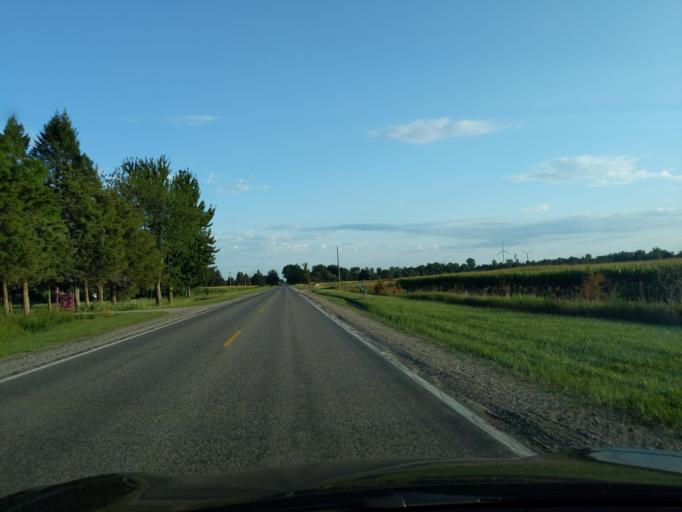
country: US
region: Michigan
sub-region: Gratiot County
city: Breckenridge
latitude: 43.4237
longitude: -84.3699
